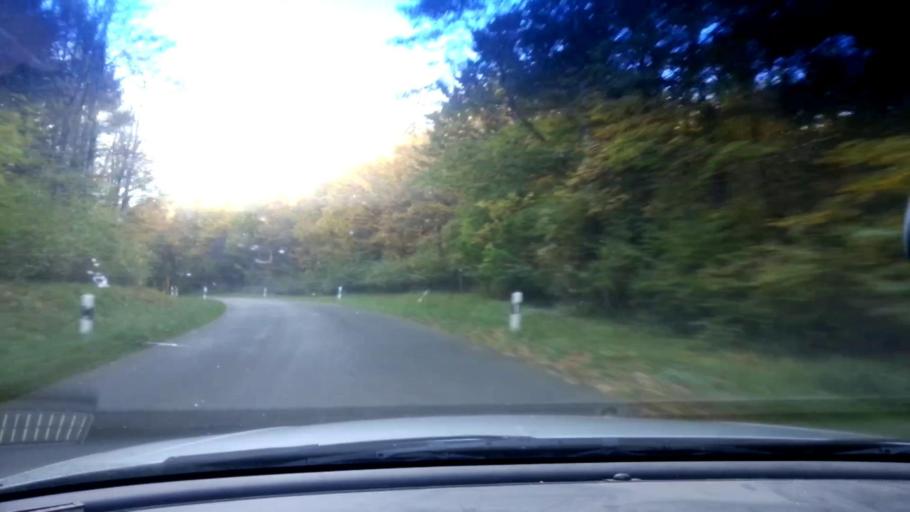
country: DE
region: Bavaria
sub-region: Upper Franconia
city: Heiligenstadt
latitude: 49.8748
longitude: 11.1841
